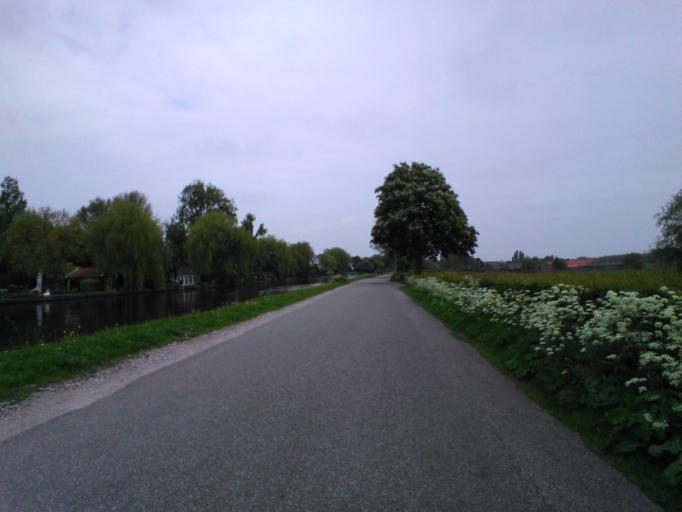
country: NL
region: South Holland
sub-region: Gemeente Voorschoten
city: Voorschoten
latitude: 52.0921
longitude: 4.4114
